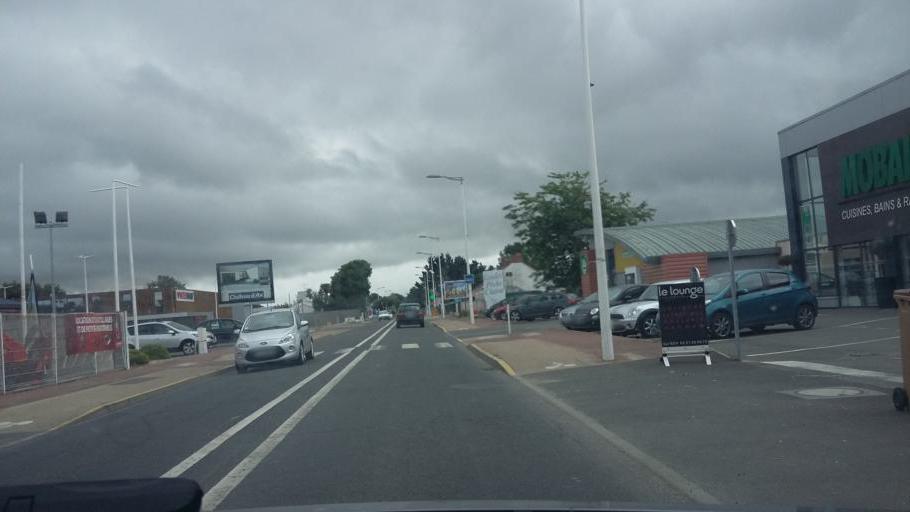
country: FR
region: Pays de la Loire
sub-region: Departement de la Vendee
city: Challans
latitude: 46.8539
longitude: -1.8949
